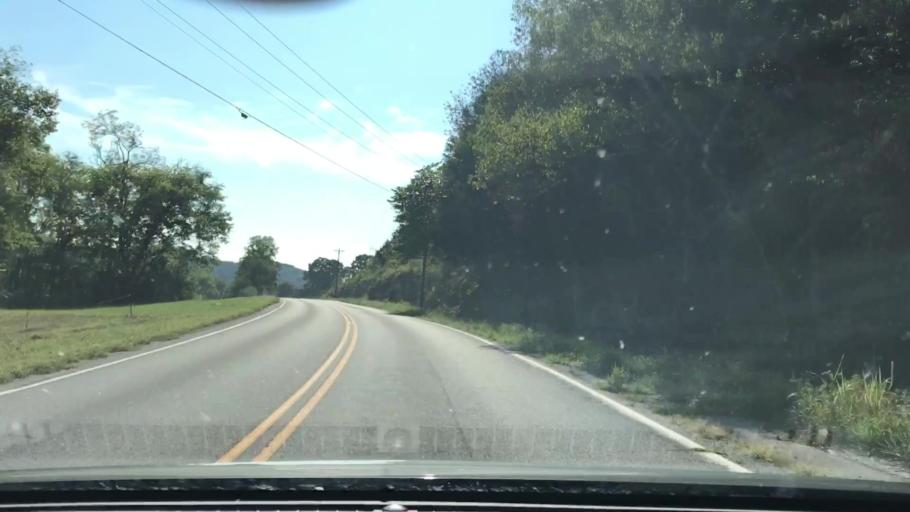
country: US
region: Tennessee
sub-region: Smith County
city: Carthage
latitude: 36.3484
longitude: -85.8218
